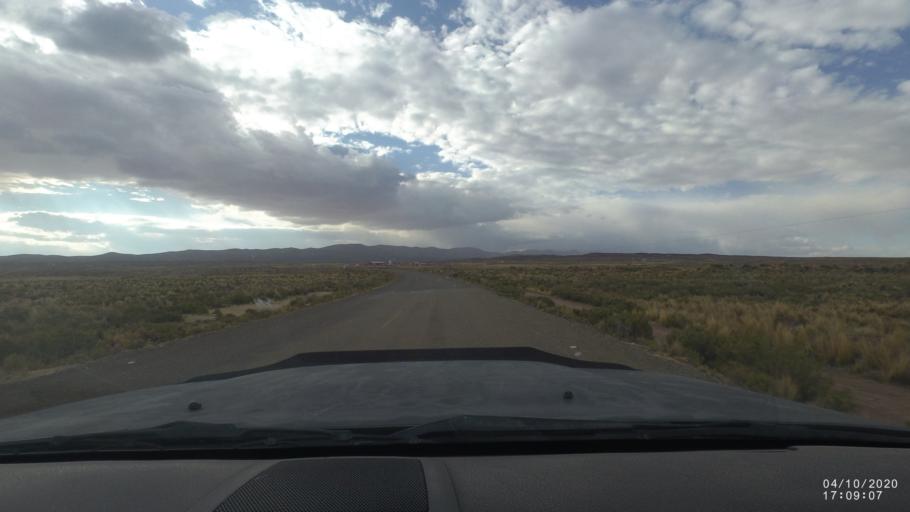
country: BO
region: Oruro
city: Oruro
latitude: -18.3415
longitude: -67.5796
